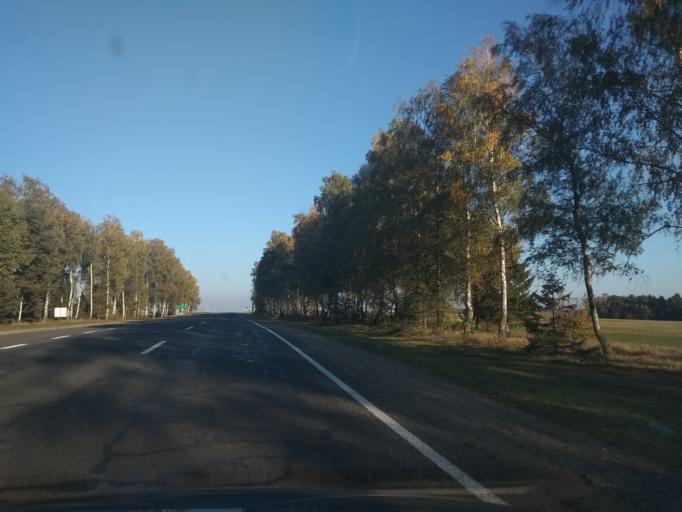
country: BY
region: Grodnenskaya
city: Svislach
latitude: 53.1277
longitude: 24.1359
